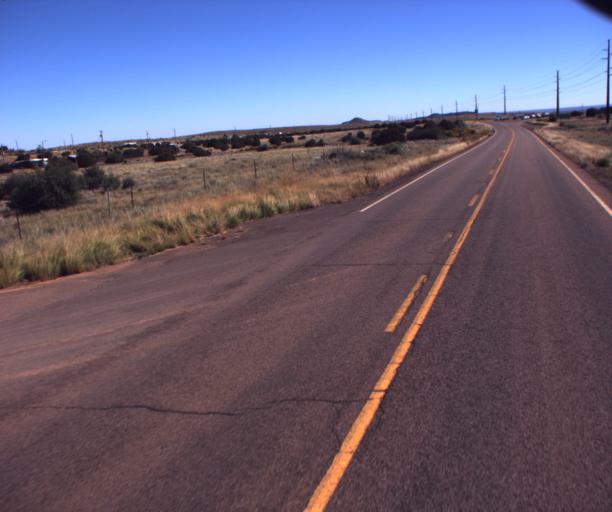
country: US
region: Arizona
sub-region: Navajo County
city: Taylor
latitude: 34.4851
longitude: -110.2478
